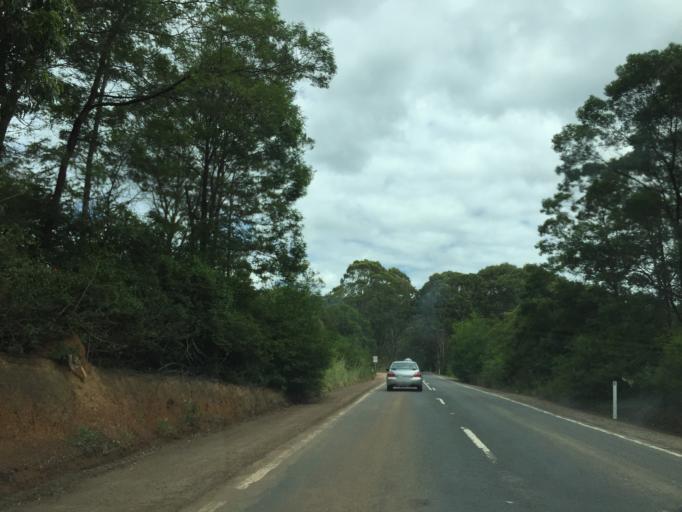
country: AU
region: New South Wales
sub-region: Hawkesbury
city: Richmond
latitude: -33.5483
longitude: 150.6691
